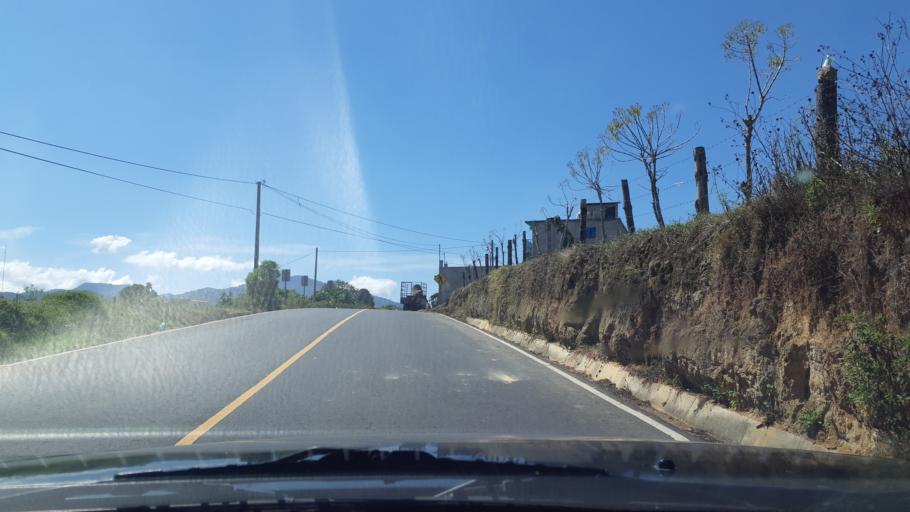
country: GT
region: Chimaltenango
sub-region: Municipio de Zaragoza
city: Zaragoza
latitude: 14.6650
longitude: -90.8620
